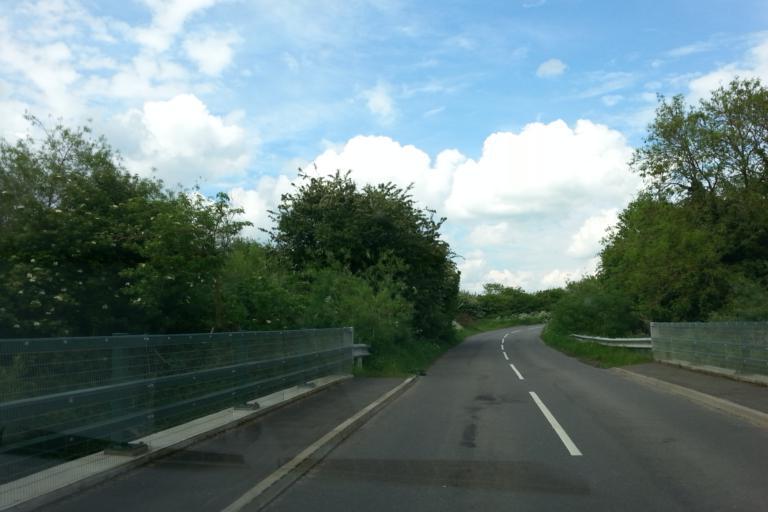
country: GB
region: England
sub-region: Lincolnshire
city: Long Bennington
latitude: 53.0006
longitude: -0.7538
